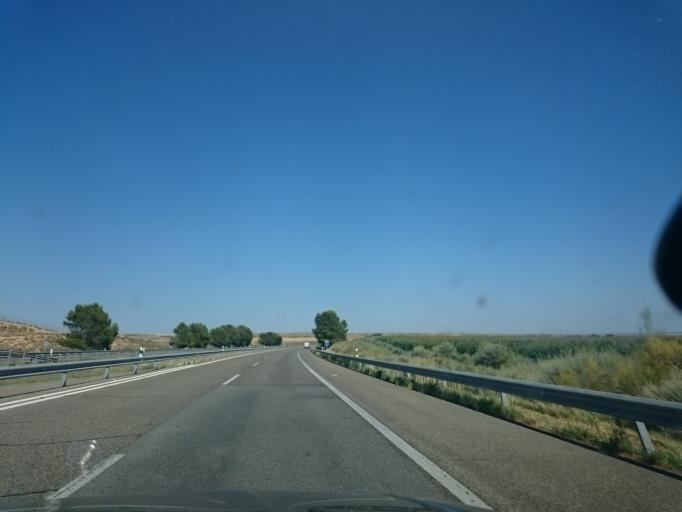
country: ES
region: Aragon
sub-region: Provincia de Huesca
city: Candasnos
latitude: 41.5251
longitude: 0.0621
